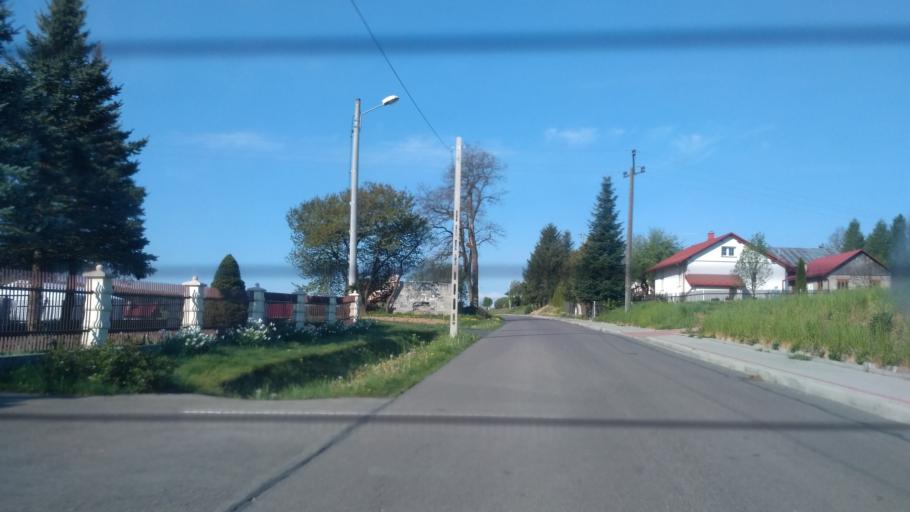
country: PL
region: Subcarpathian Voivodeship
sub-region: Powiat jaroslawski
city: Kramarzowka
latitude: 49.8575
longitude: 22.5582
